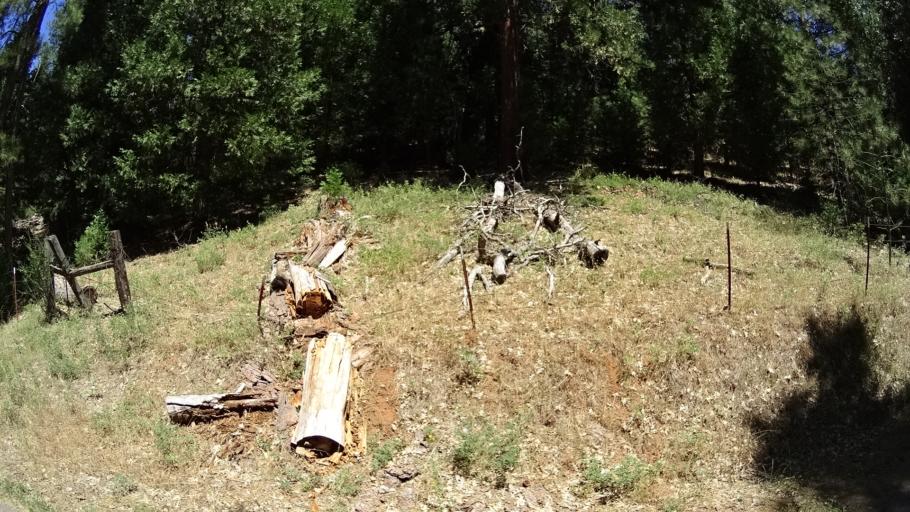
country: US
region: California
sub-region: Calaveras County
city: Mountain Ranch
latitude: 38.3279
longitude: -120.5082
